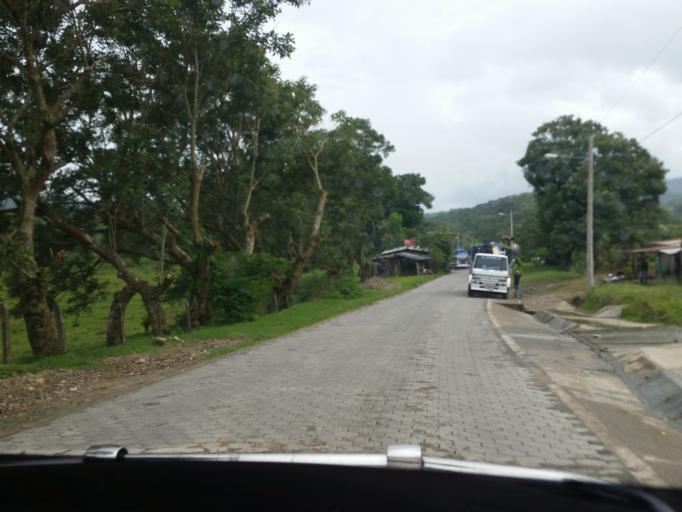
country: NI
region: Jinotega
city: Jinotega
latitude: 13.1781
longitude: -85.9140
